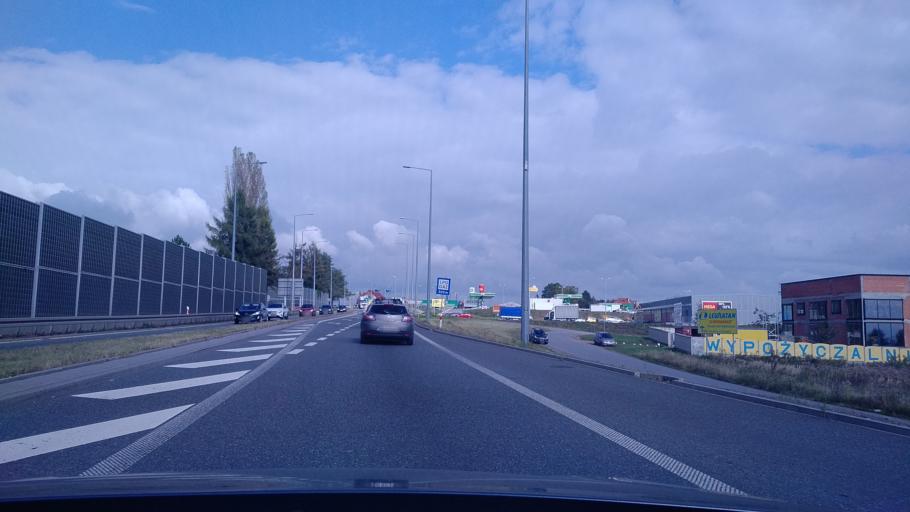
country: PL
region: Lesser Poland Voivodeship
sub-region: Powiat krakowski
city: Modlnica
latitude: 50.1236
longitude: 19.8696
